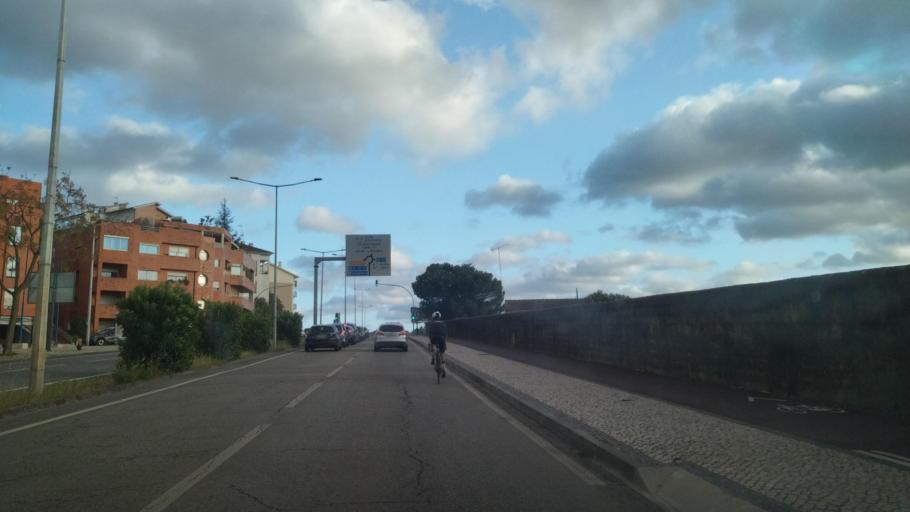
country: PT
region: Coimbra
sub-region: Coimbra
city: Coimbra
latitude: 40.1958
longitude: -8.4210
